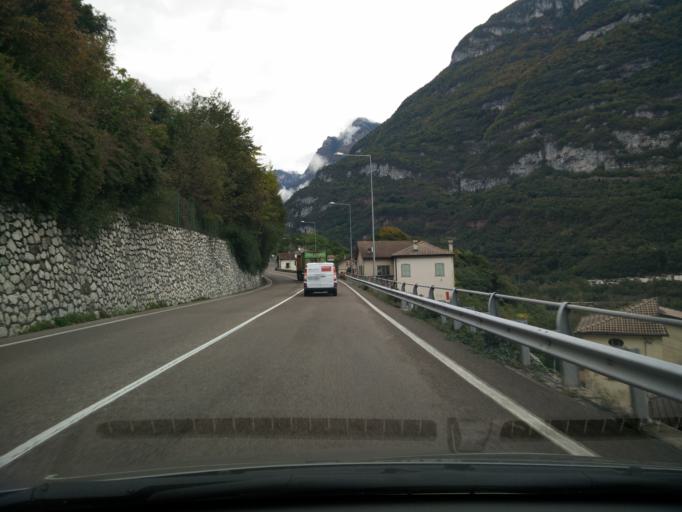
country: IT
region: Veneto
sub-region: Provincia di Belluno
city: Castello Lavazzo
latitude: 46.2771
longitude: 12.3010
